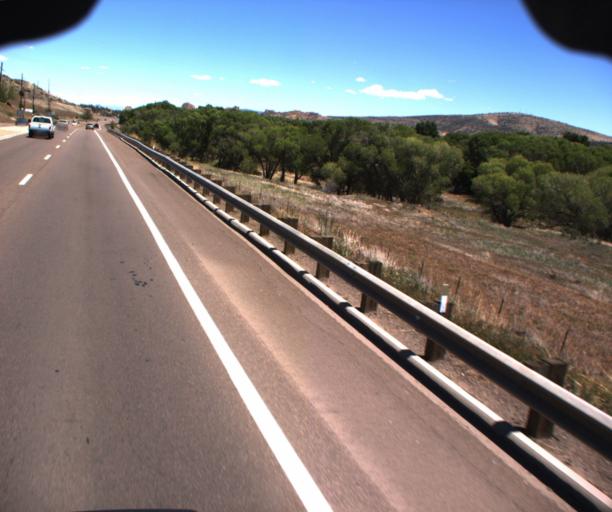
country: US
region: Arizona
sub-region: Yavapai County
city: Prescott
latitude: 34.5792
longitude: -112.4300
